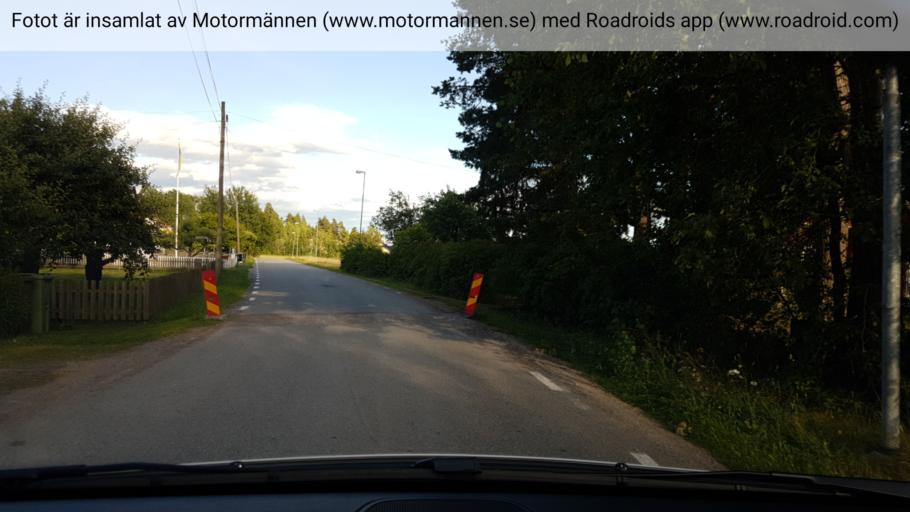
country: SE
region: Vaestmanland
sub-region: Vasteras
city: Tillberga
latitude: 59.6927
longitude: 16.6029
